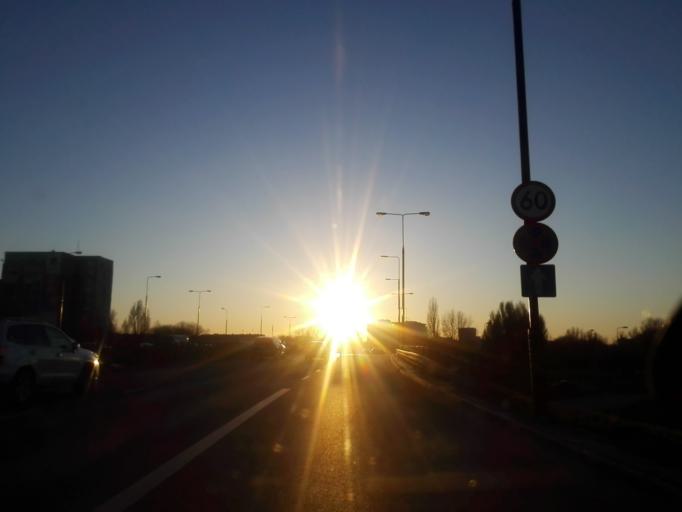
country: PL
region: Masovian Voivodeship
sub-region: Warszawa
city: Ursynow
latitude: 52.1663
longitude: 21.0282
